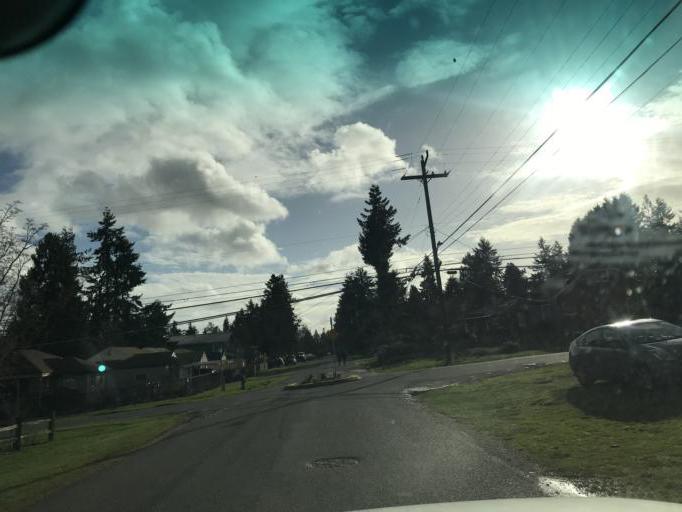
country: US
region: Washington
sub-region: King County
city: Lake Forest Park
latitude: 47.7160
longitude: -122.3072
